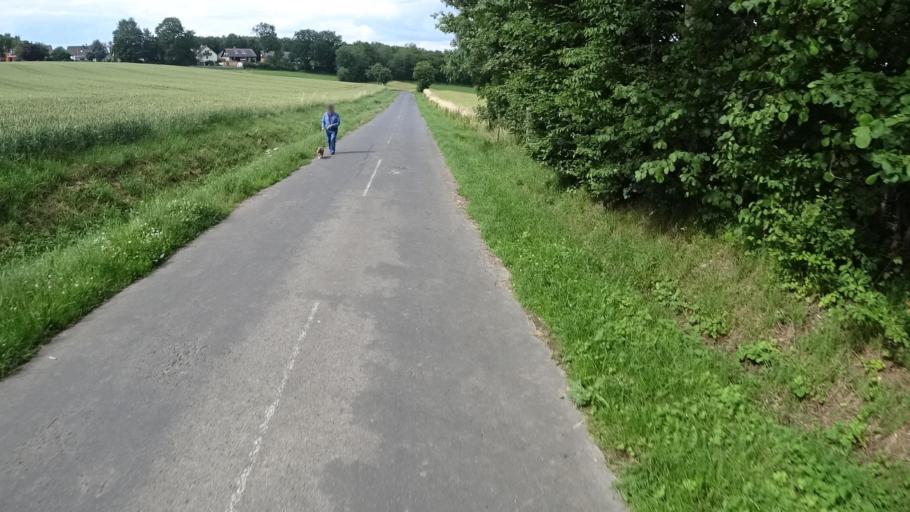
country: DE
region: Rheinland-Pfalz
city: Vettelschoss
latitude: 50.6039
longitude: 7.3374
